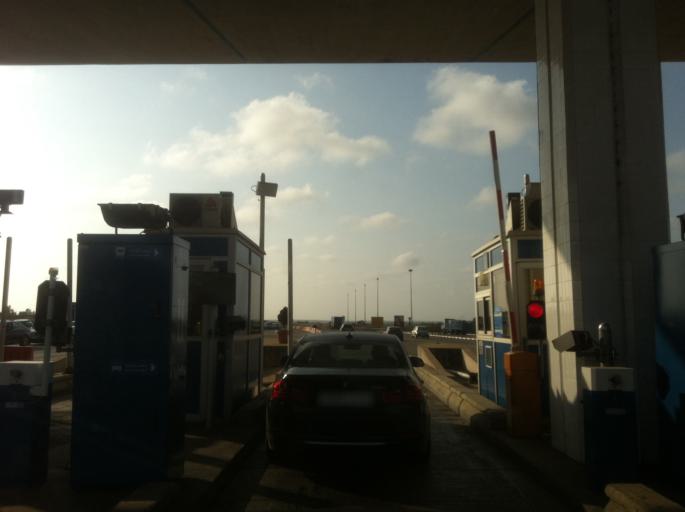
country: MA
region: Gharb-Chrarda-Beni Hssen
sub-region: Kenitra Province
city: Kenitra
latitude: 34.2293
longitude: -6.5241
